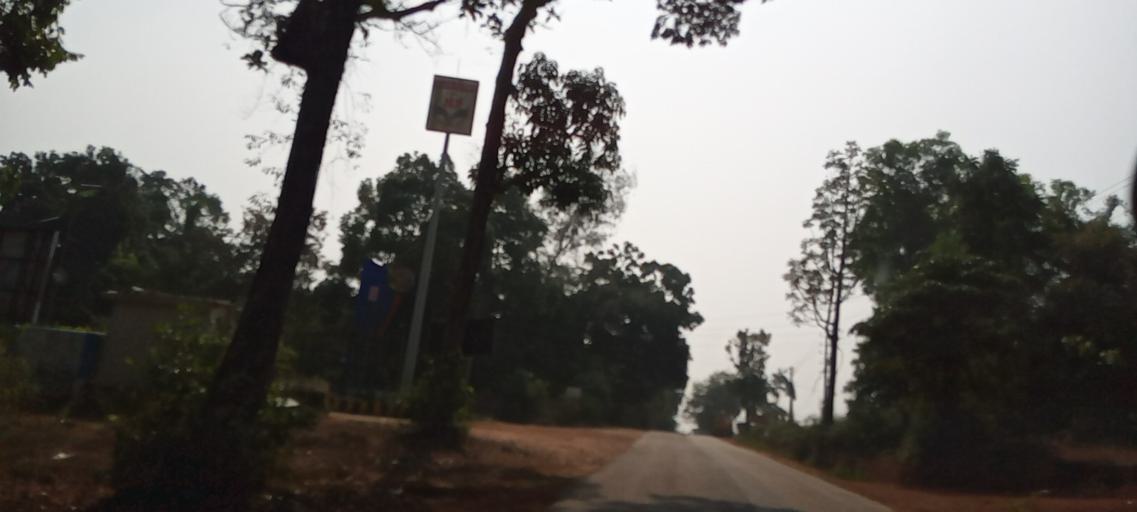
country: IN
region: Karnataka
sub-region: Udupi
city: Someshwar
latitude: 13.5318
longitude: 74.9180
